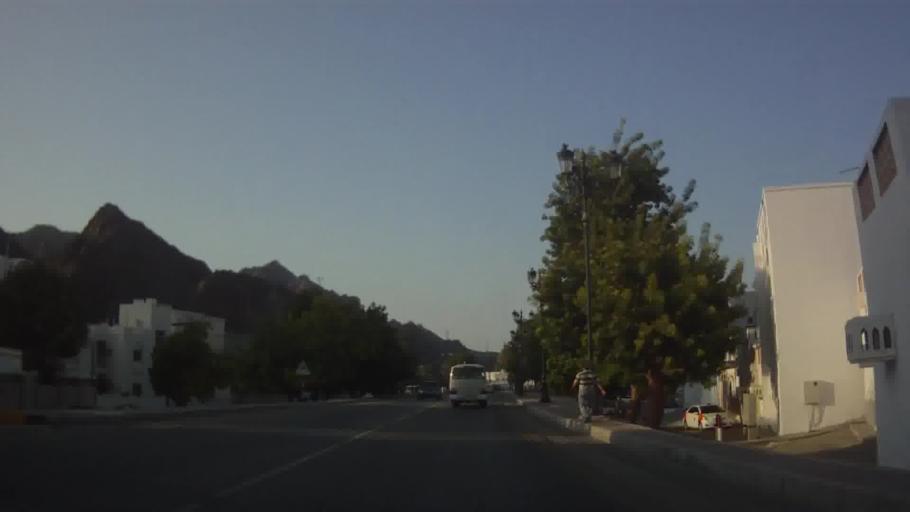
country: OM
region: Muhafazat Masqat
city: Muscat
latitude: 23.5963
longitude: 58.5975
